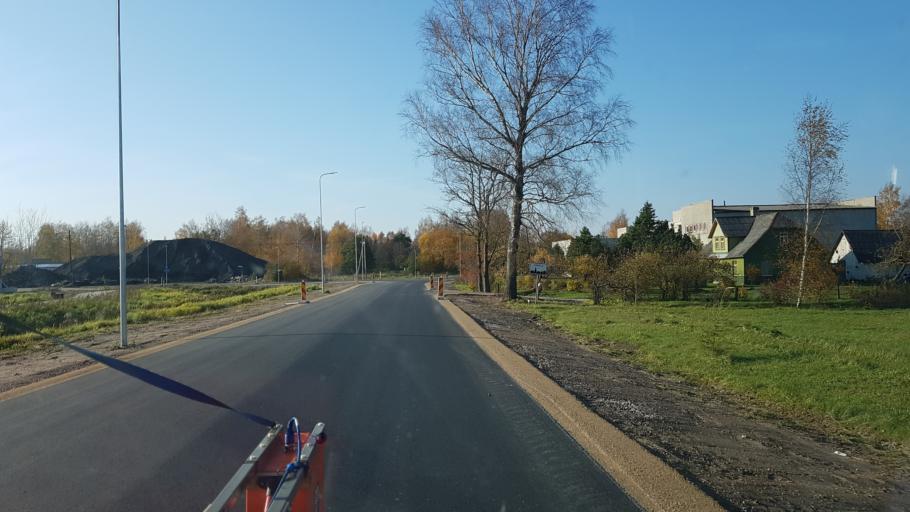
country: EE
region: Vorumaa
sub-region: Antsla vald
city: Vana-Antsla
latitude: 57.8397
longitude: 26.4843
